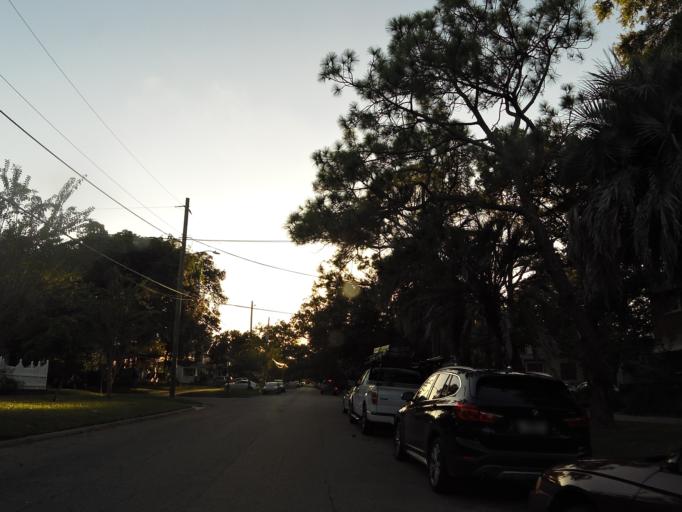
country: US
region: Florida
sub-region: Duval County
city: Jacksonville
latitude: 30.3167
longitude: -81.6856
